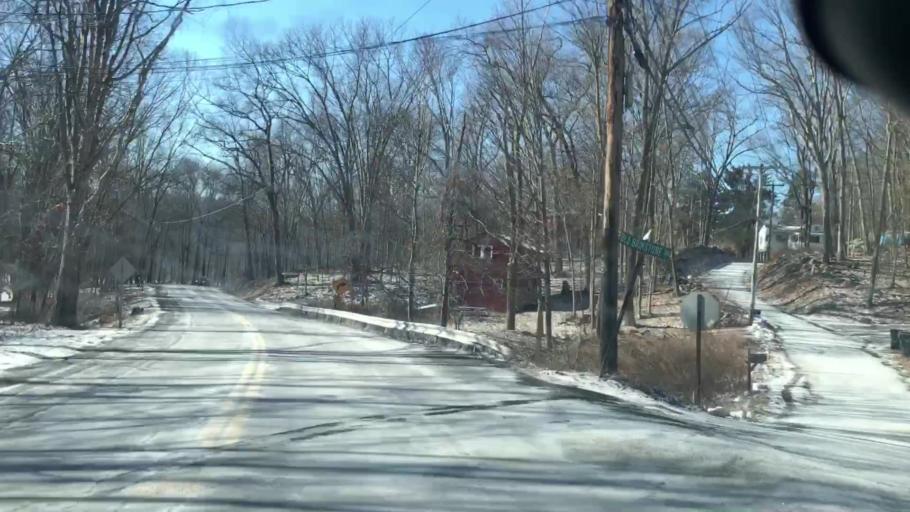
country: US
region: New York
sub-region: Putnam County
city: Carmel Hamlet
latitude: 41.3873
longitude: -73.6699
